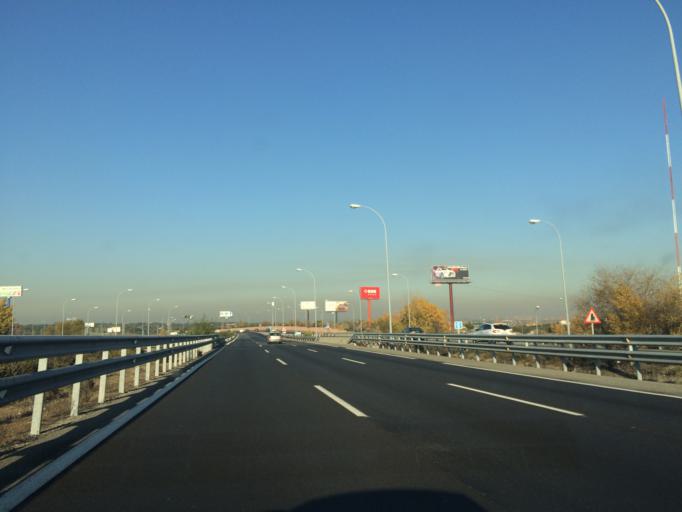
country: ES
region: Madrid
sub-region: Provincia de Madrid
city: Pozuelo de Alarcon
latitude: 40.4352
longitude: -3.8342
